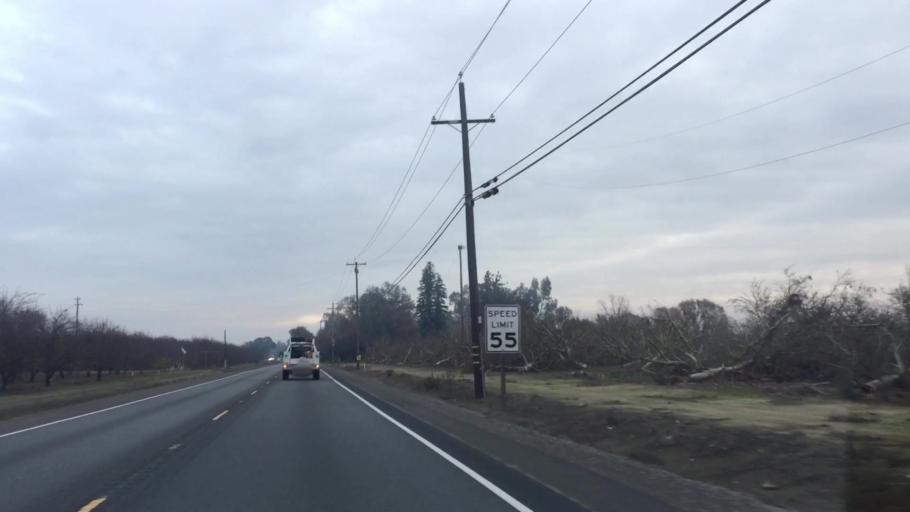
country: US
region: California
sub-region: Sutter County
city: Live Oak
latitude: 39.2684
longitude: -121.5966
